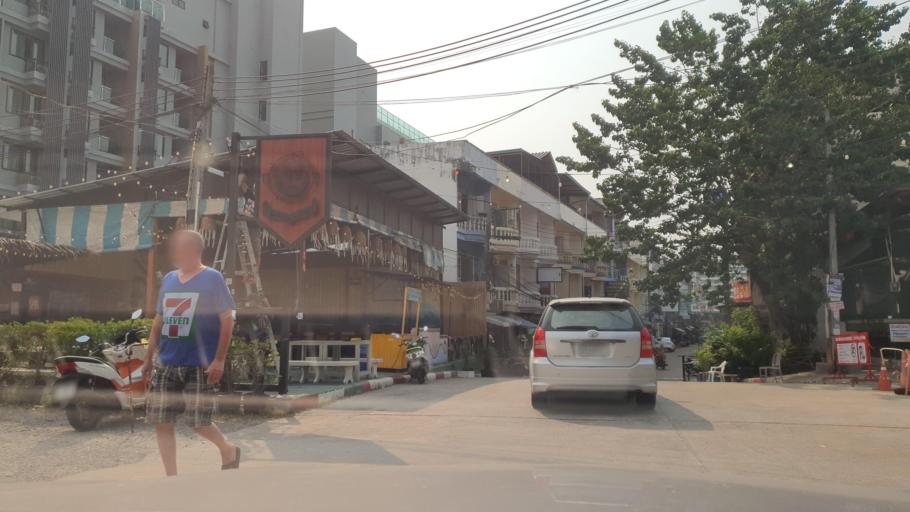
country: TH
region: Chon Buri
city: Phatthaya
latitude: 12.9312
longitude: 100.8850
